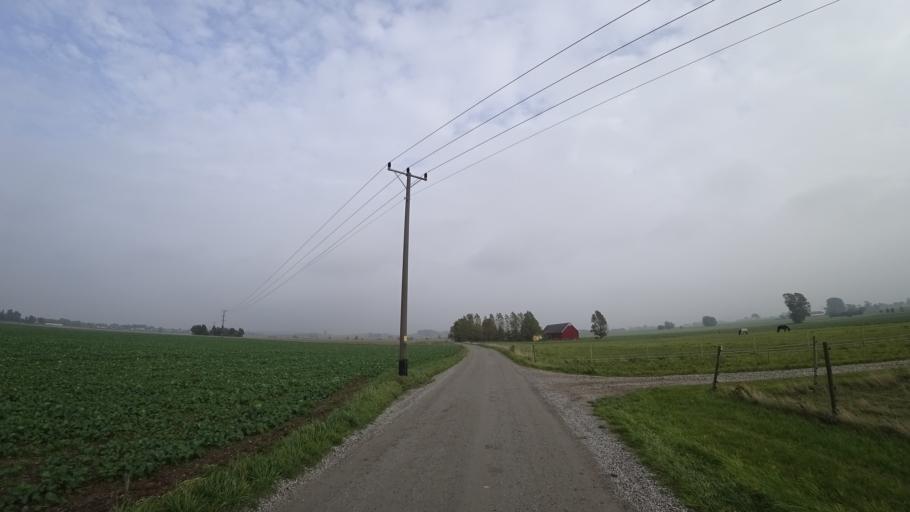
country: SE
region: Skane
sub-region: Kavlinge Kommun
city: Loddekopinge
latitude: 55.8094
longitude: 13.0096
